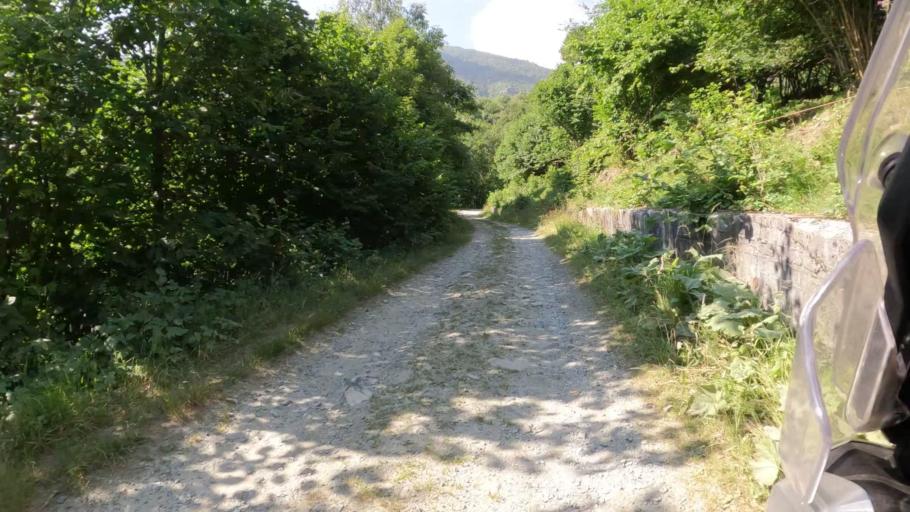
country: IT
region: Piedmont
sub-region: Provincia di Torino
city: Lemie
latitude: 45.2049
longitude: 7.3053
